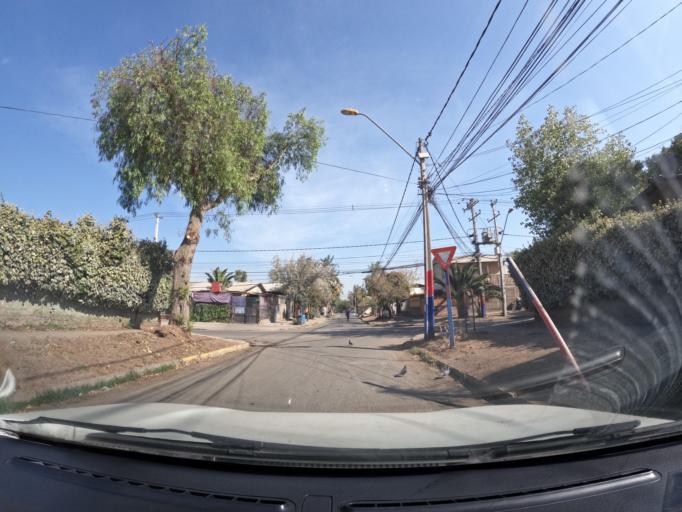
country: CL
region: Santiago Metropolitan
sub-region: Provincia de Santiago
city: Villa Presidente Frei, Nunoa, Santiago, Chile
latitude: -33.4648
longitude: -70.5538
